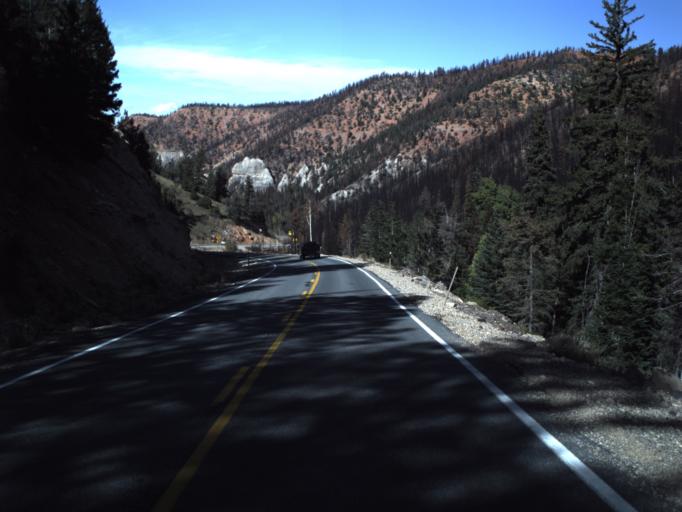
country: US
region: Utah
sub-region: Iron County
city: Parowan
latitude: 37.7228
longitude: -112.8430
